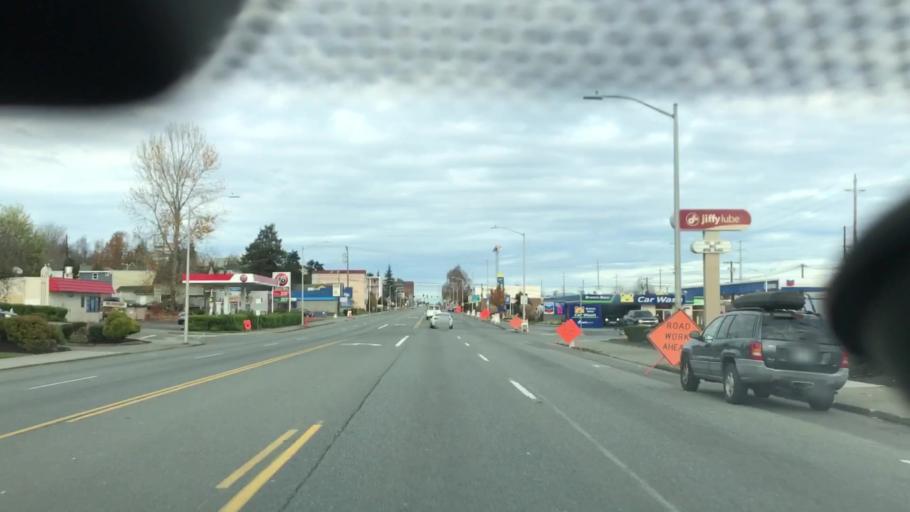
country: US
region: Washington
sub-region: Snohomish County
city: Everett
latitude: 47.9696
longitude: -122.2012
